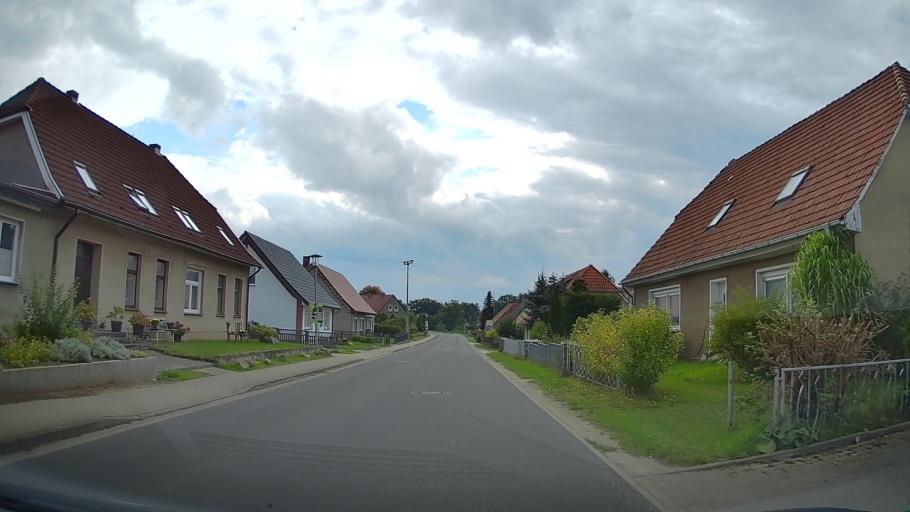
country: DE
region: Mecklenburg-Vorpommern
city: Lubtheen
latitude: 53.3963
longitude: 10.9658
